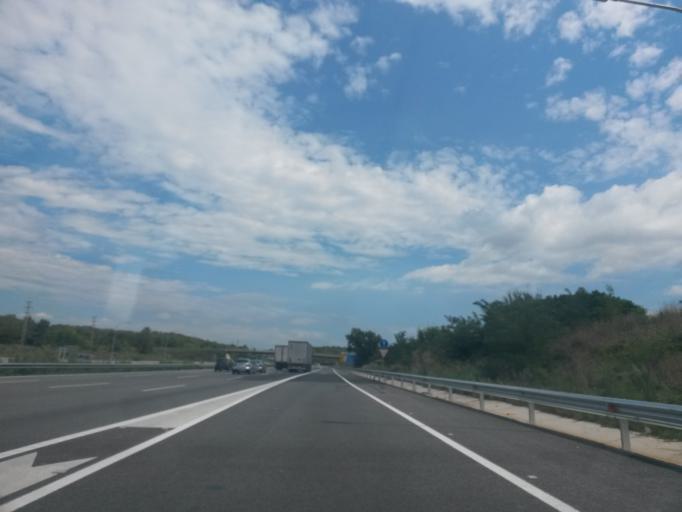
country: ES
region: Catalonia
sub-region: Provincia de Girona
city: Salt
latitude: 41.9948
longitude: 2.7958
